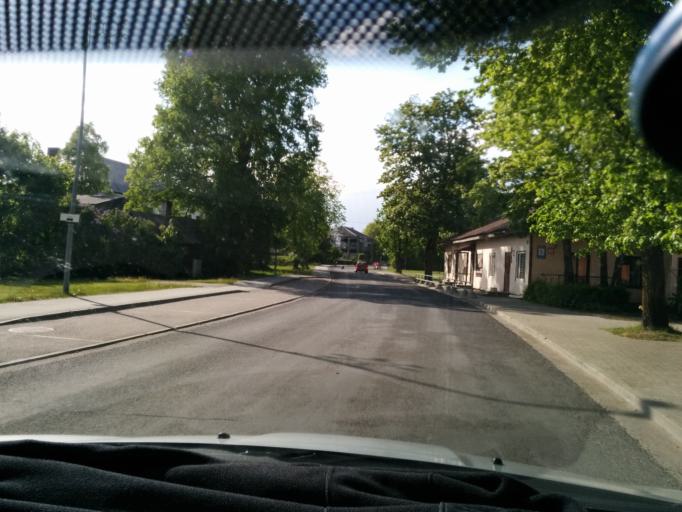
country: EE
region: Harju
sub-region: Loksa linn
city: Loksa
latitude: 59.5811
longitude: 25.7218
